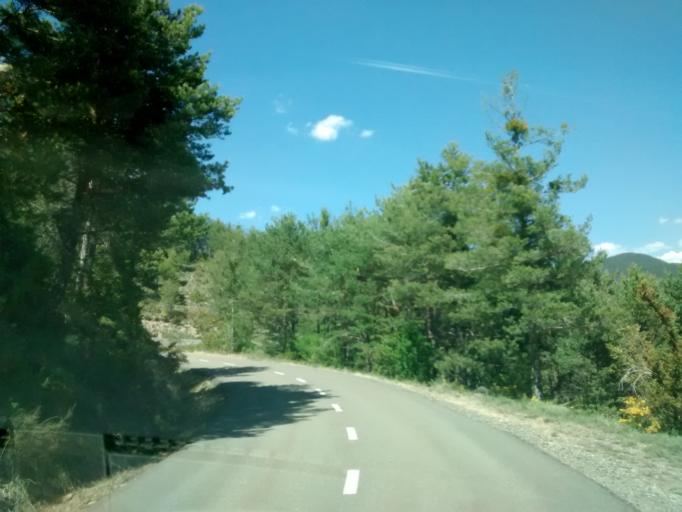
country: ES
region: Aragon
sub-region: Provincia de Huesca
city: Borau
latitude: 42.6679
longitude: -0.5959
